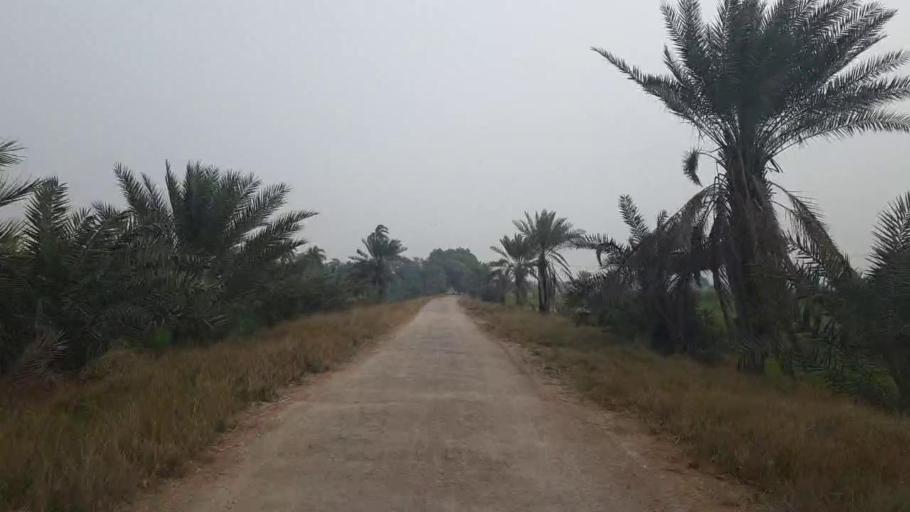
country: PK
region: Sindh
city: Tando Adam
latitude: 25.8130
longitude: 68.6660
